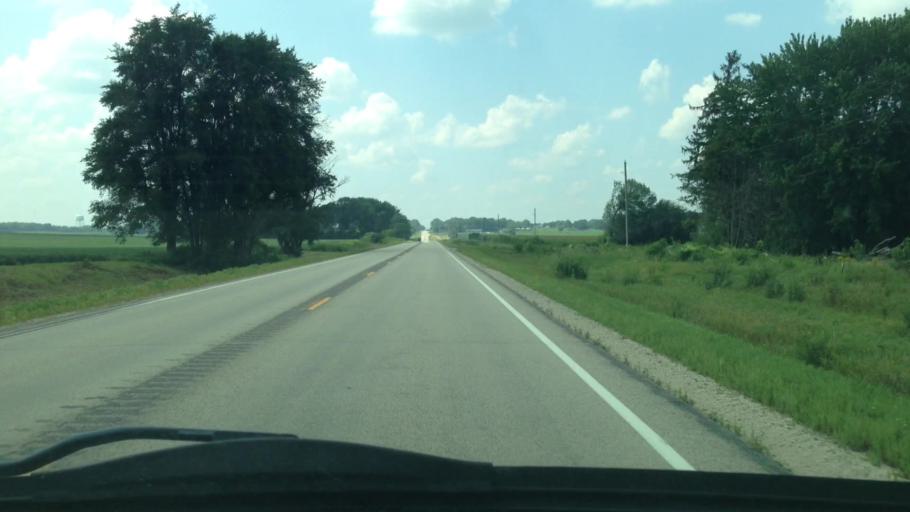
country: US
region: Minnesota
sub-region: Olmsted County
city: Stewartville
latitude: 43.8556
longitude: -92.4503
